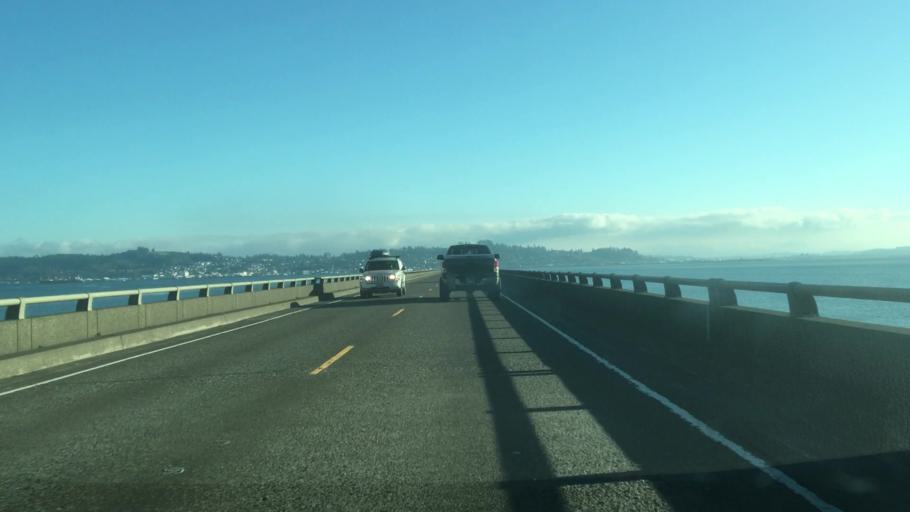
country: US
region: Oregon
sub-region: Clatsop County
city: Astoria
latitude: 46.2251
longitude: -123.8670
